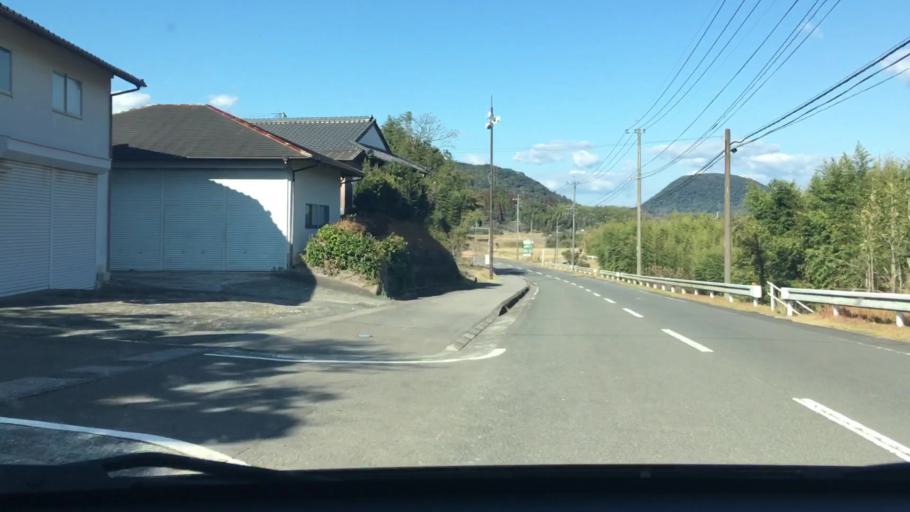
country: JP
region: Kagoshima
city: Satsumasendai
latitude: 31.7733
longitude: 130.4013
